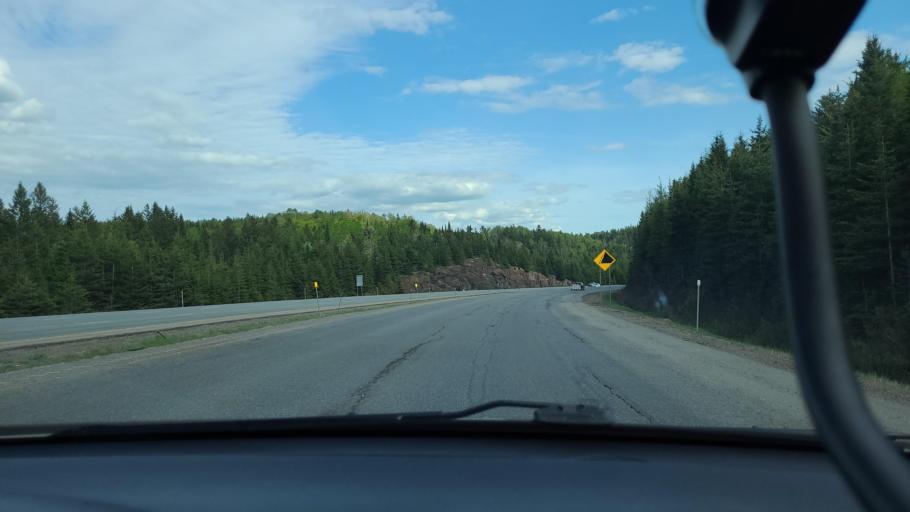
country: CA
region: Quebec
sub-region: Laurentides
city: Val-David
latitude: 46.0234
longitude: -74.2378
